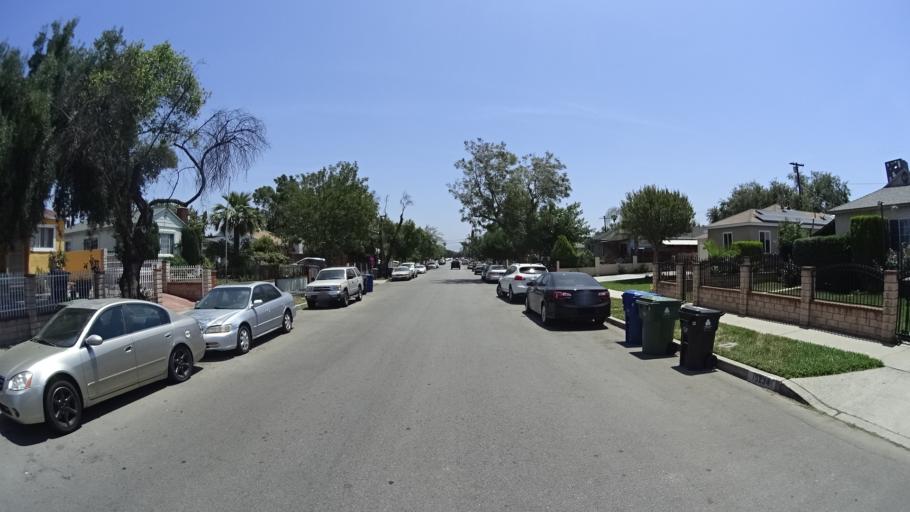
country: US
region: California
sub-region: Los Angeles County
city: Van Nuys
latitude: 34.2181
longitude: -118.4652
